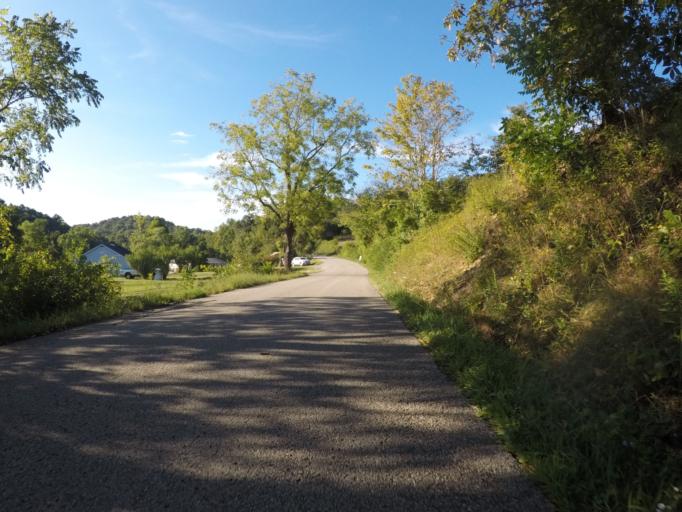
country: US
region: West Virginia
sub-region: Cabell County
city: Huntington
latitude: 38.5176
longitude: -82.5010
